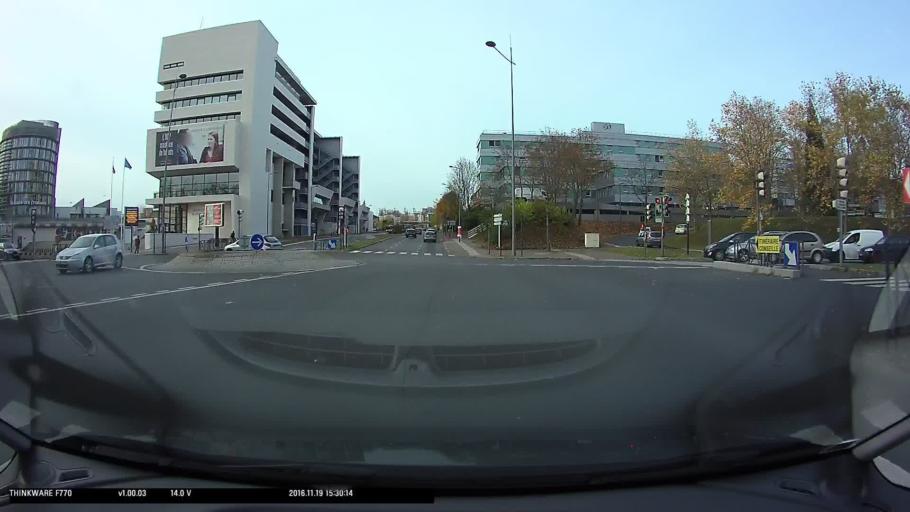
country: FR
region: Ile-de-France
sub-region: Departement du Val-d'Oise
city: Cergy-Pontoise
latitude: 49.0388
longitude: 2.0774
